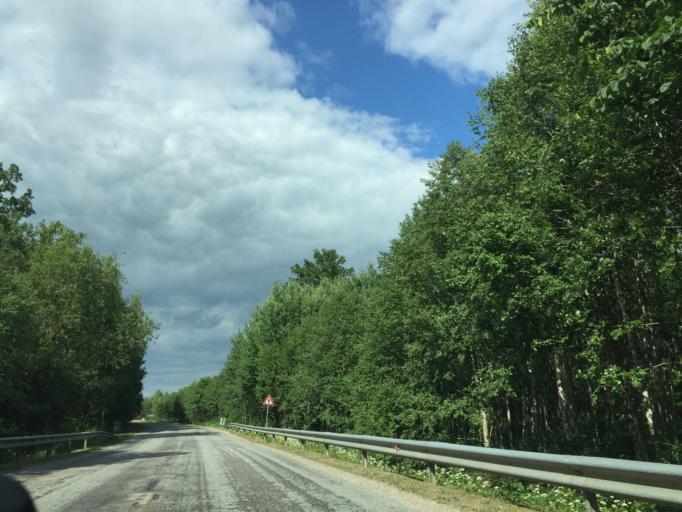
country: LV
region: Skriveri
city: Skriveri
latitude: 56.8079
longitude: 25.1108
